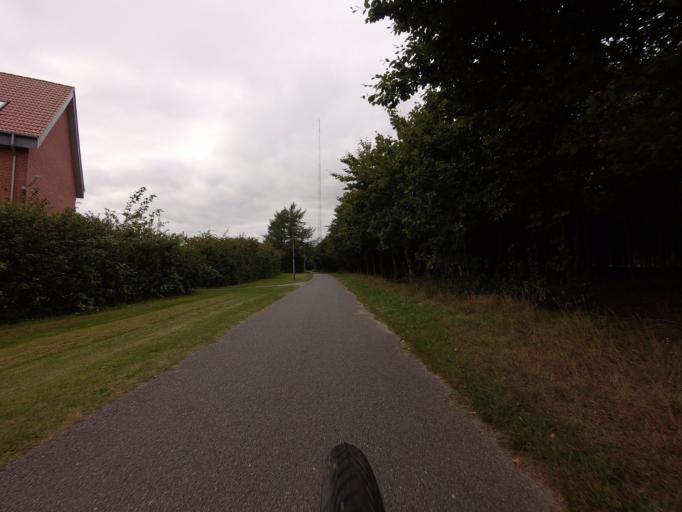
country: DK
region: South Denmark
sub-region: Billund Kommune
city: Grindsted
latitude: 55.7647
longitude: 8.9235
